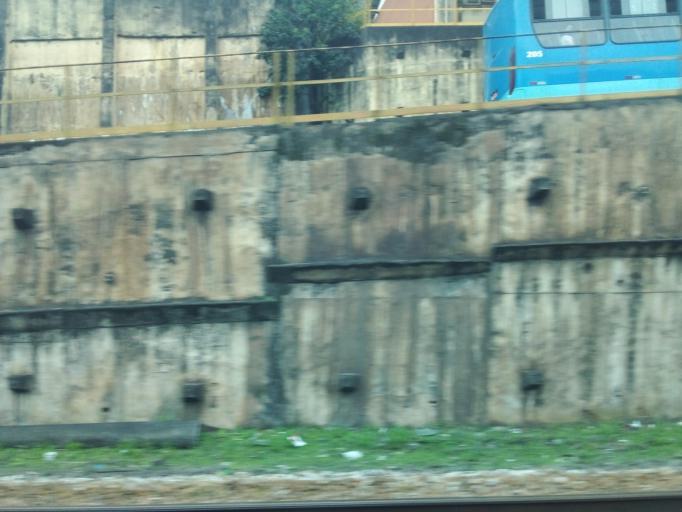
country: BR
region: Minas Gerais
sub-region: Joao Monlevade
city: Joao Monlevade
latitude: -19.8346
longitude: -43.1293
